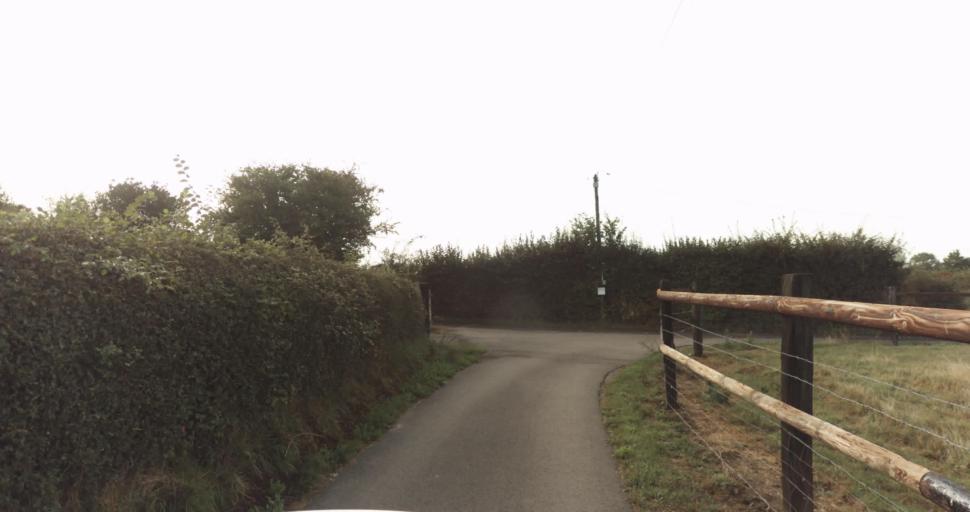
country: FR
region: Lower Normandy
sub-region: Departement de l'Orne
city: Gace
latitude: 48.9006
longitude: 0.3044
